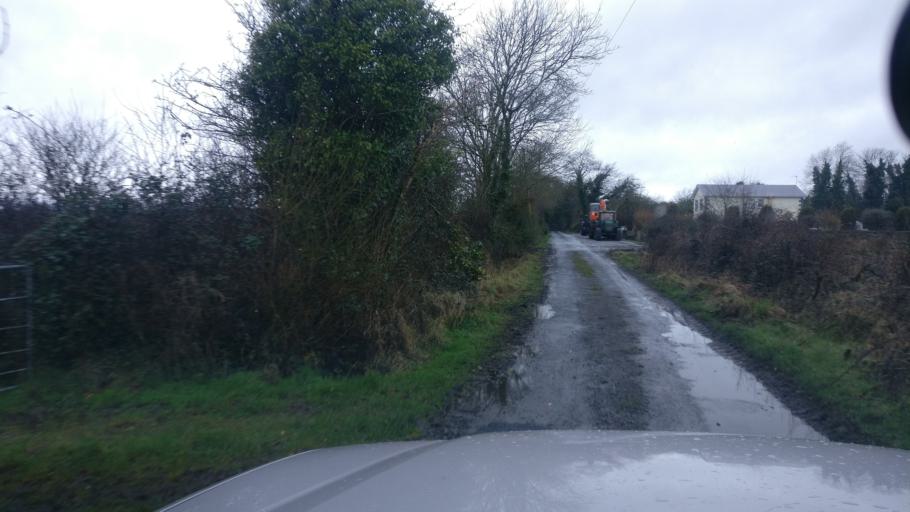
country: IE
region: Connaught
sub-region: County Galway
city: Ballinasloe
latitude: 53.2518
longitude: -8.3348
